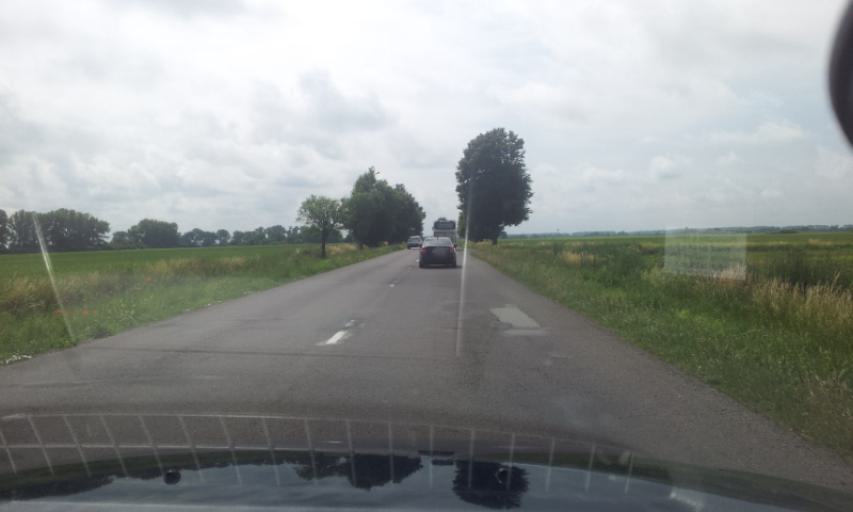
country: SK
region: Kosicky
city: Michalovce
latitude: 48.7276
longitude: 21.9569
